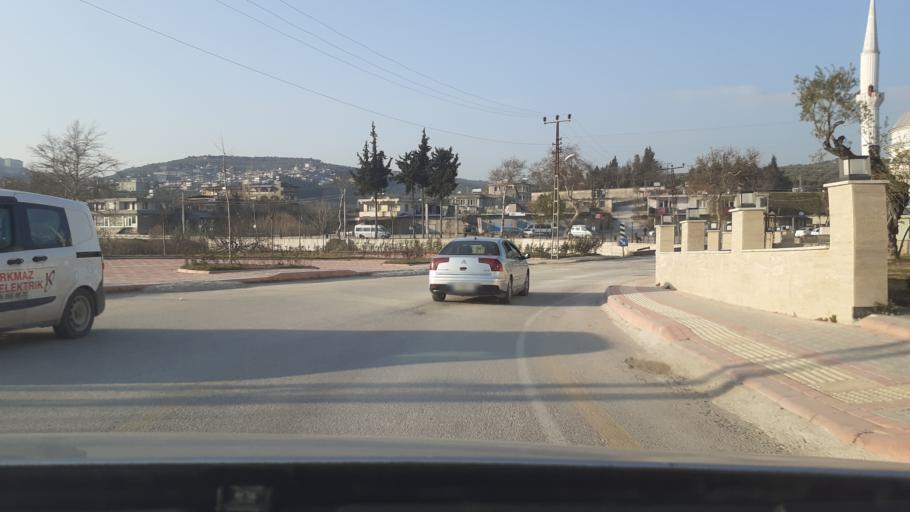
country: TR
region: Hatay
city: Fatikli
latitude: 36.1120
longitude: 36.2621
